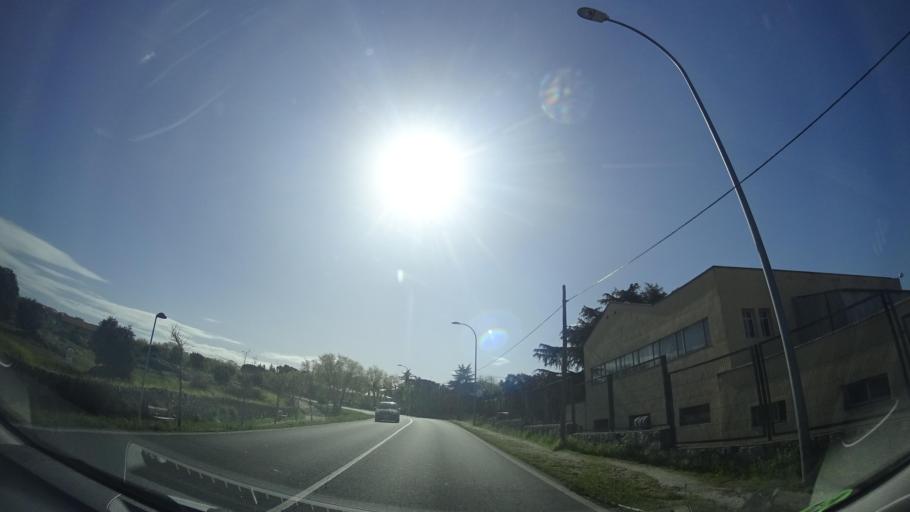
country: ES
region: Madrid
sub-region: Provincia de Madrid
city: Colmenar Viejo
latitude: 40.6537
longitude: -3.7844
